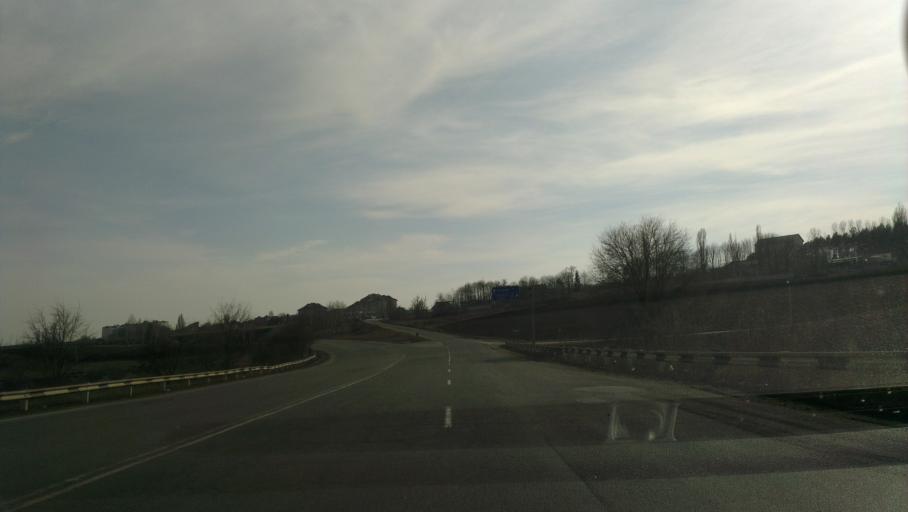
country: MD
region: Laloveni
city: Ialoveni
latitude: 46.9672
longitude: 28.7542
